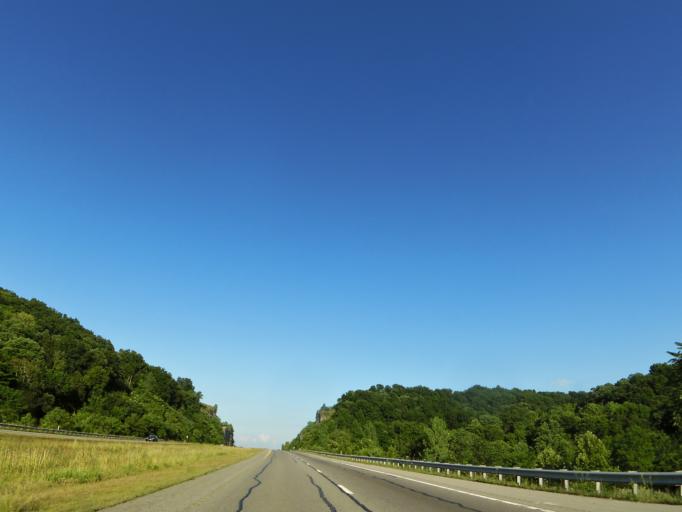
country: US
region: Tennessee
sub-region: Williamson County
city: Thompson's Station
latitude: 35.8154
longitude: -86.8075
